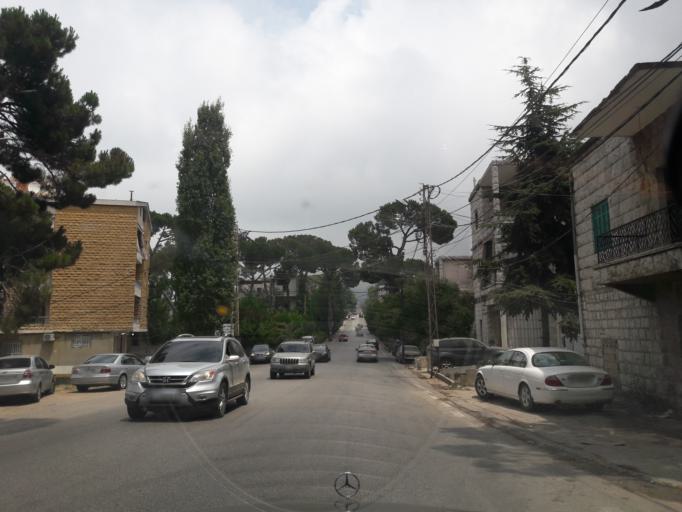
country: LB
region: Mont-Liban
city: Bhamdoun el Mhatta
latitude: 33.9117
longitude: 35.7431
